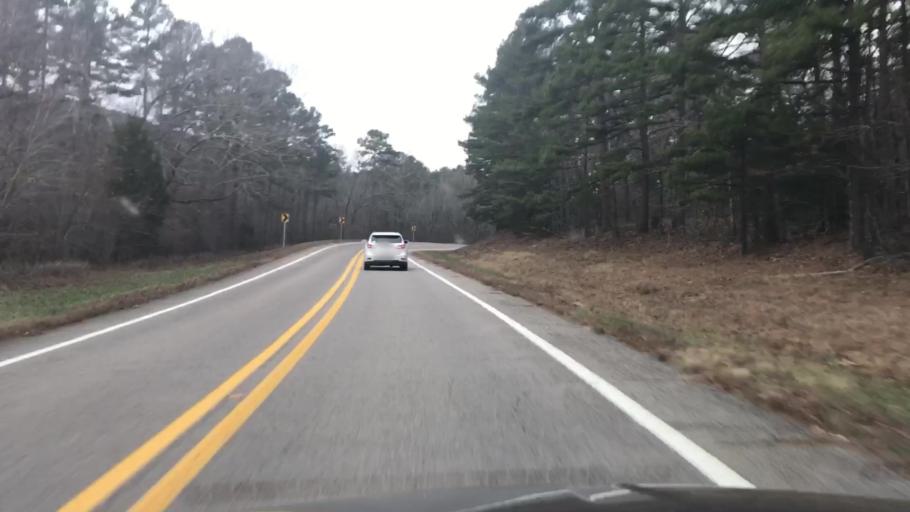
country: US
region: Arkansas
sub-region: Montgomery County
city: Mount Ida
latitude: 34.6860
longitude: -93.8717
